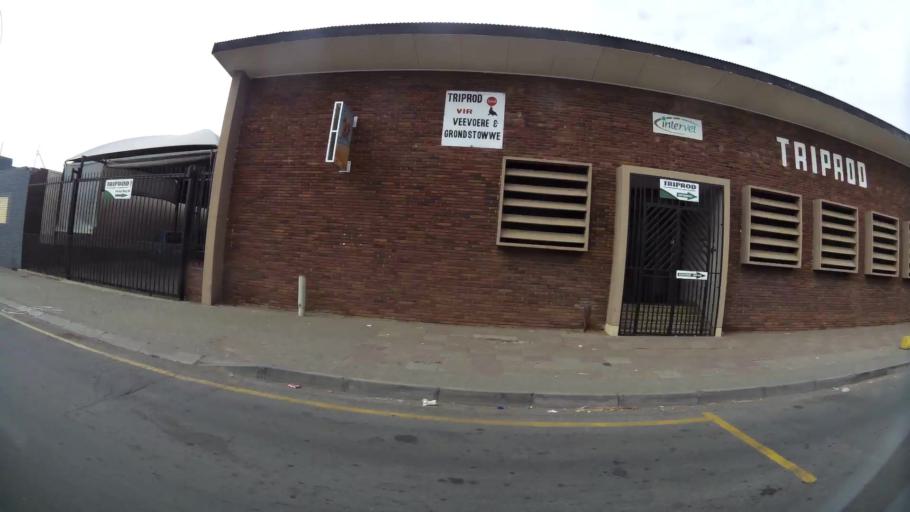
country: ZA
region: Orange Free State
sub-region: Mangaung Metropolitan Municipality
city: Bloemfontein
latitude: -29.1354
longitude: 26.2182
